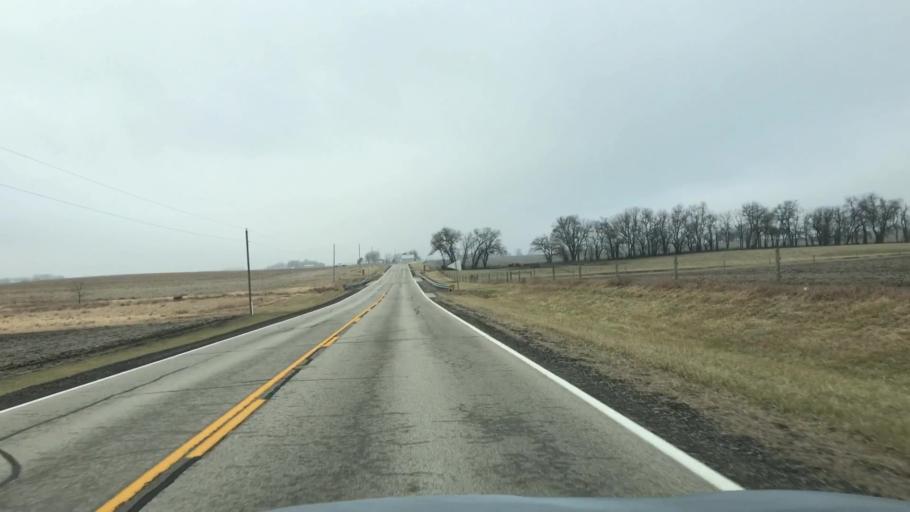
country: US
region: Illinois
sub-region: McLean County
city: Hudson
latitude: 40.6276
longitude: -88.9401
